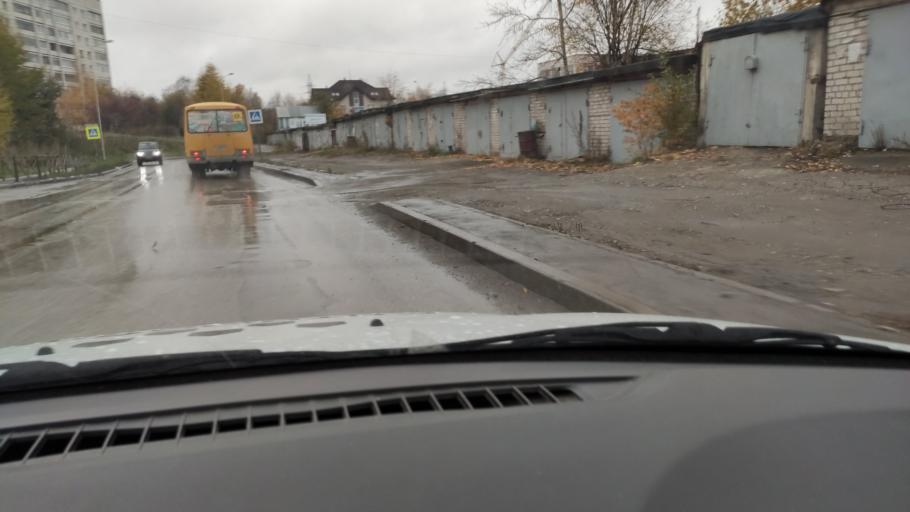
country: RU
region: Perm
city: Perm
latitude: 57.9799
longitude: 56.2813
